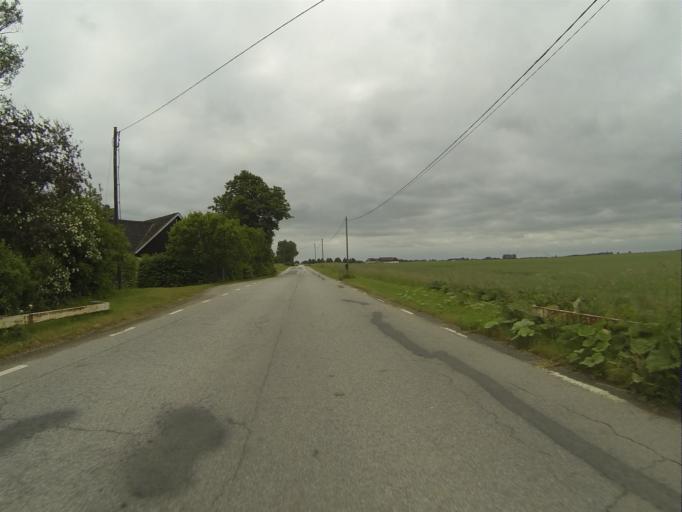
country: SE
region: Skane
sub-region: Staffanstorps Kommun
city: Staffanstorp
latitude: 55.6579
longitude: 13.2600
